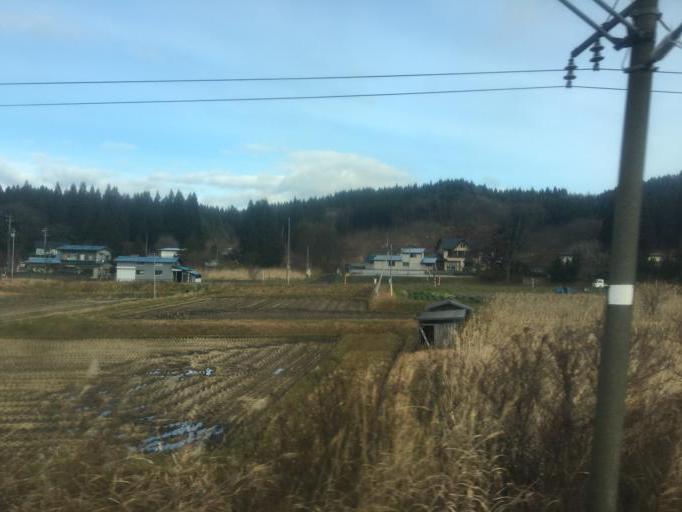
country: JP
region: Akita
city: Takanosu
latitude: 40.2633
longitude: 140.4256
